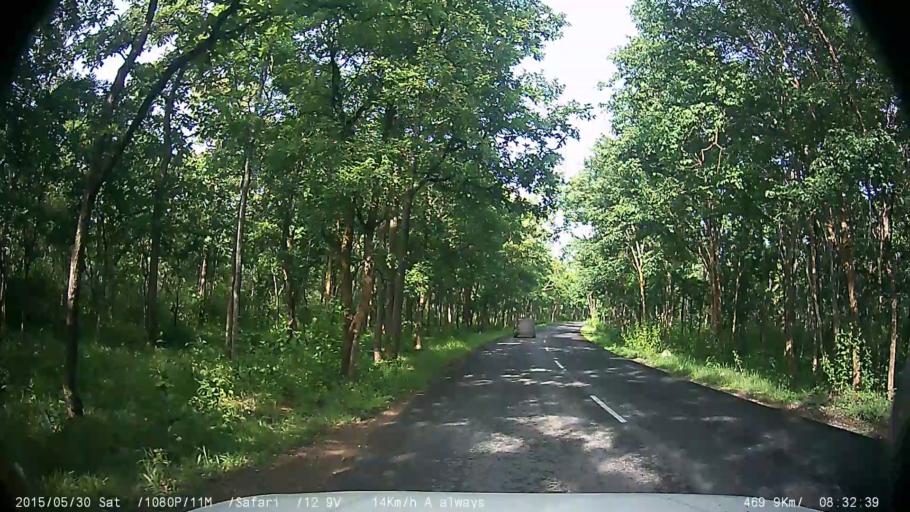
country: IN
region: Tamil Nadu
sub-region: Nilgiri
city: Masinigudi
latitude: 11.7293
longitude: 76.4526
